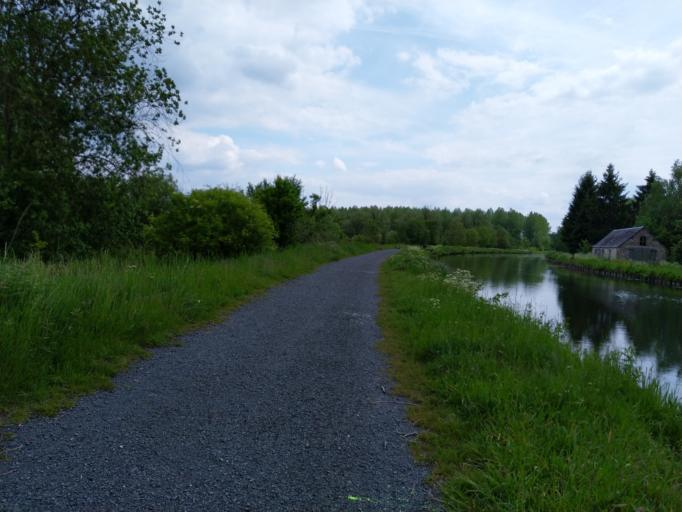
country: FR
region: Nord-Pas-de-Calais
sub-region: Departement du Nord
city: Landrecies
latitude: 50.0757
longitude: 3.6468
